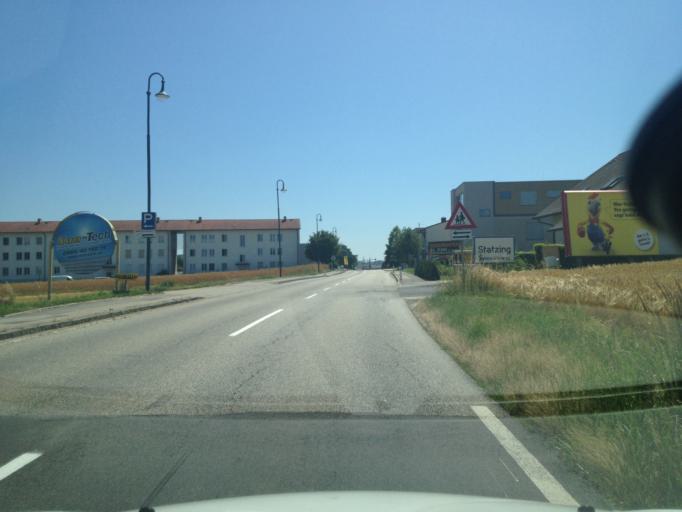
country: AT
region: Upper Austria
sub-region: Politischer Bezirk Linz-Land
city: Asten
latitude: 48.2726
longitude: 14.4245
